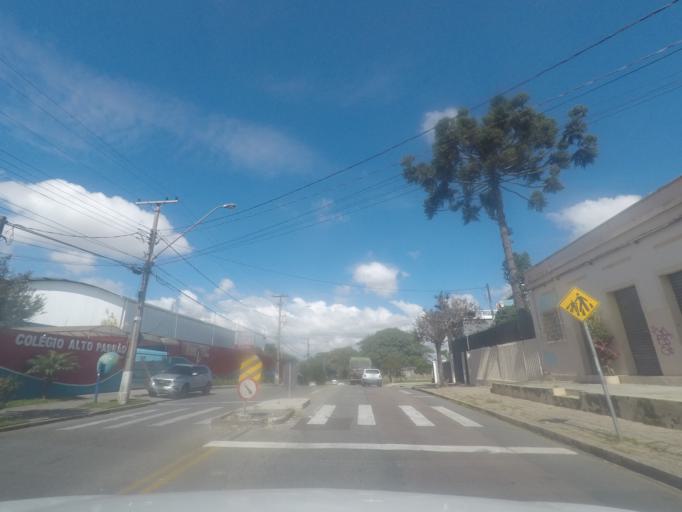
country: BR
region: Parana
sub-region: Pinhais
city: Pinhais
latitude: -25.4431
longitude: -49.2321
